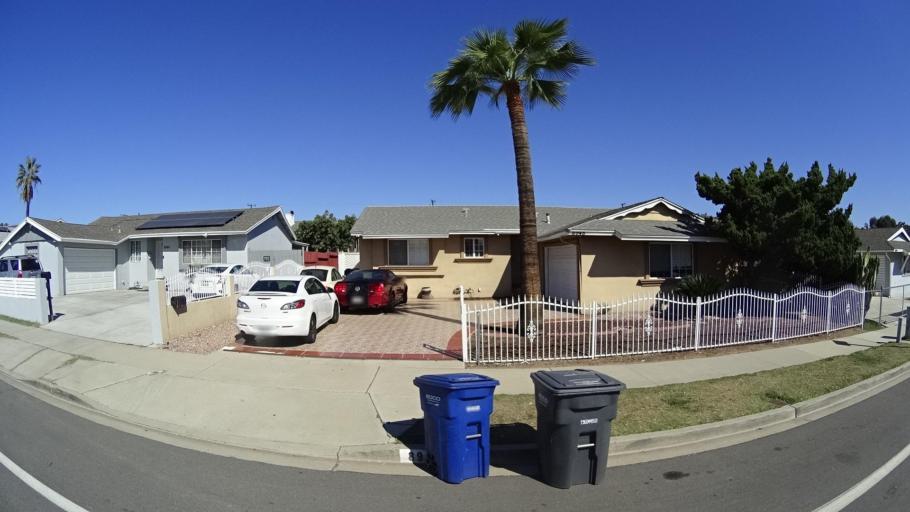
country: US
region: California
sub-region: San Diego County
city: La Presa
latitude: 32.7078
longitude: -117.0061
